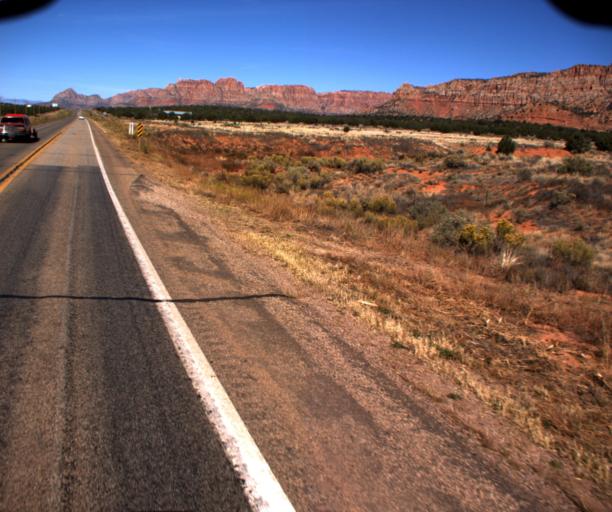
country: US
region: Arizona
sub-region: Mohave County
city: Colorado City
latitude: 36.9475
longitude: -112.9565
